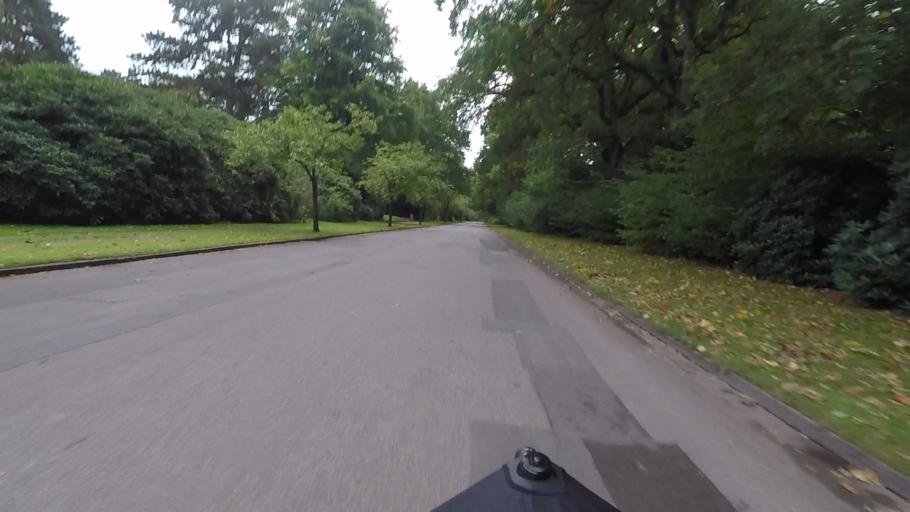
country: DE
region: Hamburg
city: Wellingsbuettel
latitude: 53.6265
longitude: 10.0732
